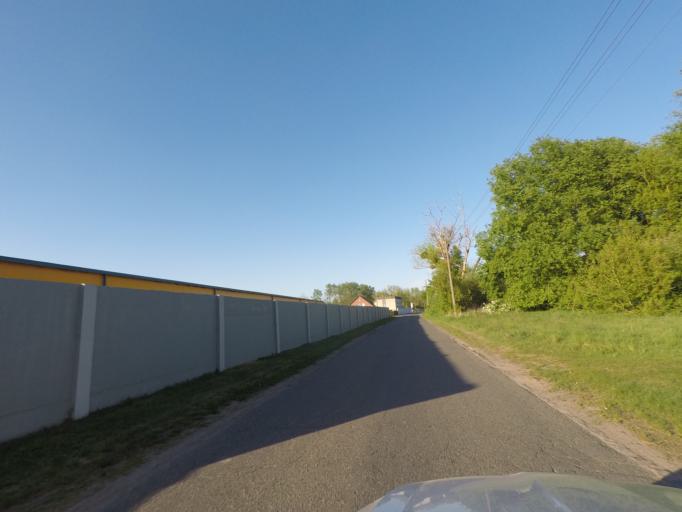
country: DE
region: Brandenburg
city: Oderberg
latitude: 52.8409
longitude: 14.0145
